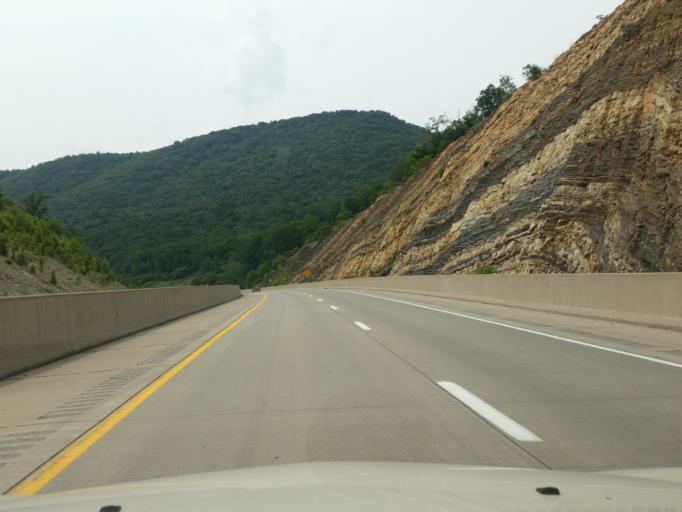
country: US
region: Pennsylvania
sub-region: Juniata County
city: Mifflintown
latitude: 40.6095
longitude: -77.4395
